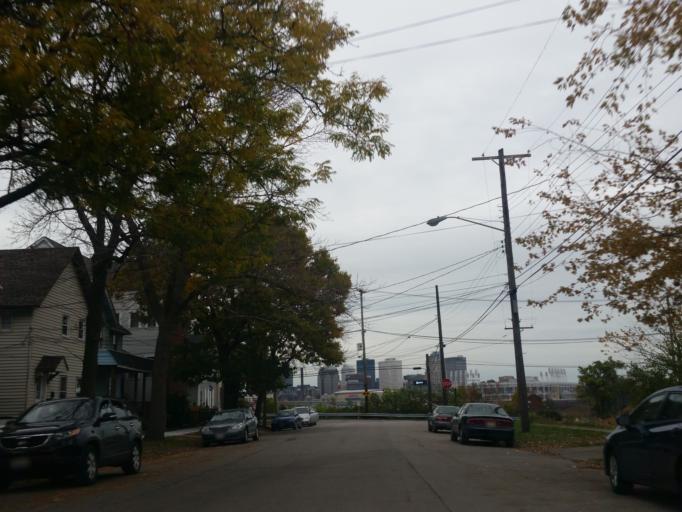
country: US
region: Ohio
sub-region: Cuyahoga County
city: Cleveland
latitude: 41.4840
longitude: -81.6876
